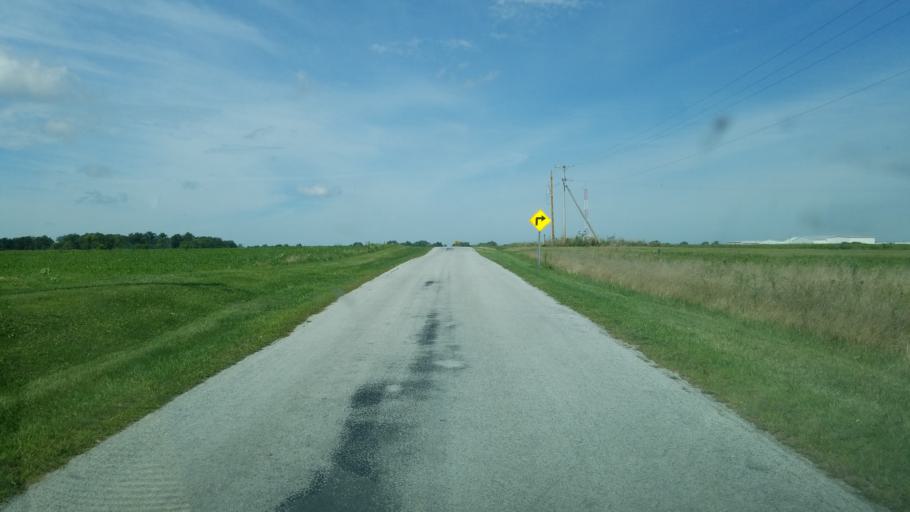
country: US
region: Ohio
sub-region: Hardin County
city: Kenton
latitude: 40.6135
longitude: -83.6364
